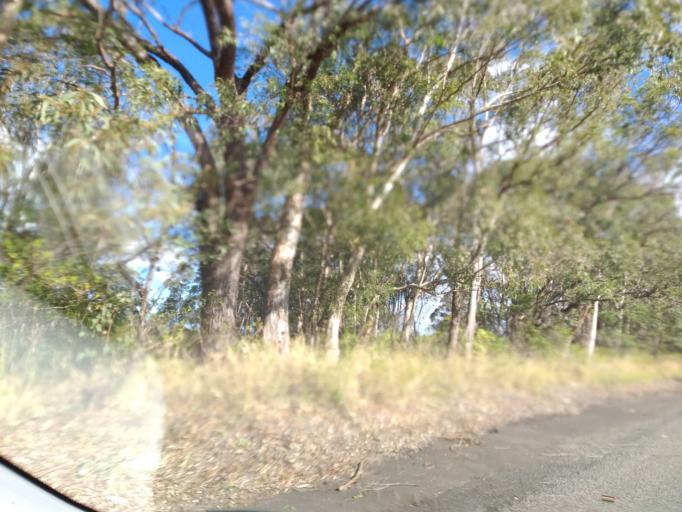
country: AU
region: New South Wales
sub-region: Shellharbour
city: Albion Park Rail
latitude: -34.5374
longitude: 150.7829
